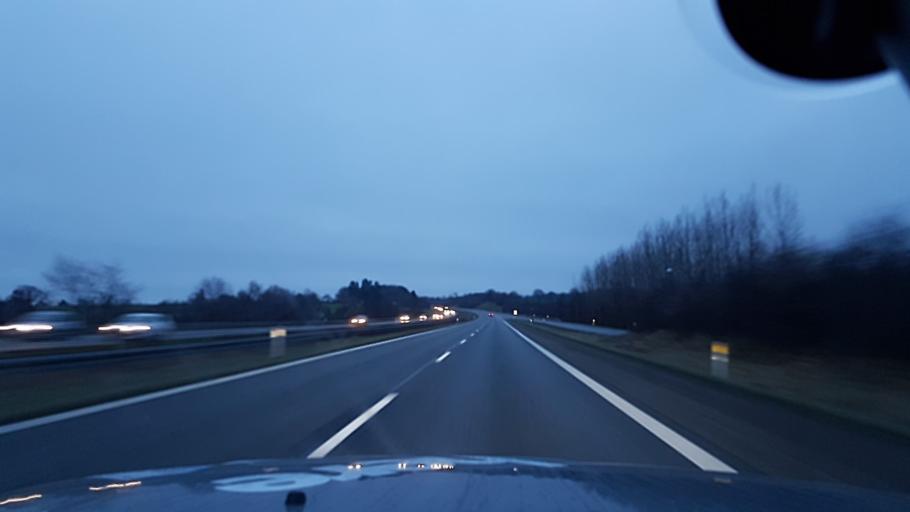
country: DK
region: Zealand
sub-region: Faxe Kommune
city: Ronnede
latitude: 55.3253
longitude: 12.0357
